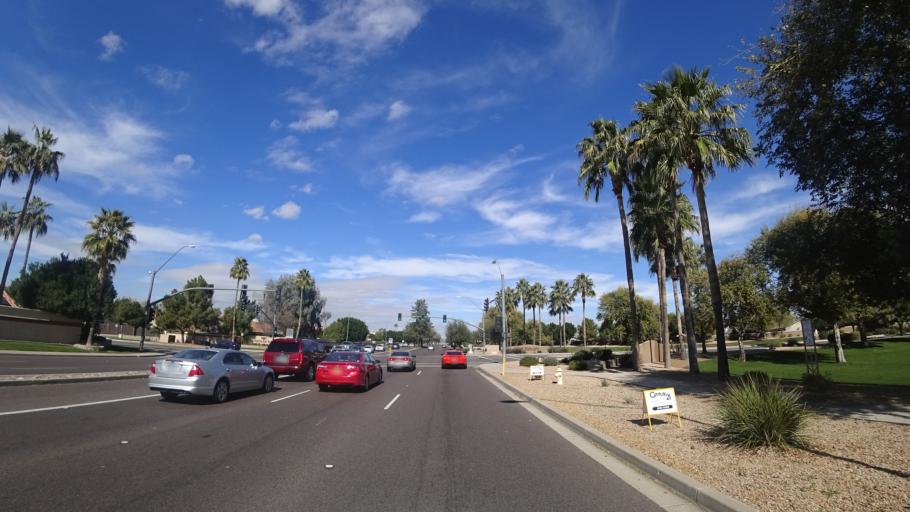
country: US
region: Arizona
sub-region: Maricopa County
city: Peoria
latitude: 33.6597
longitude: -112.2029
